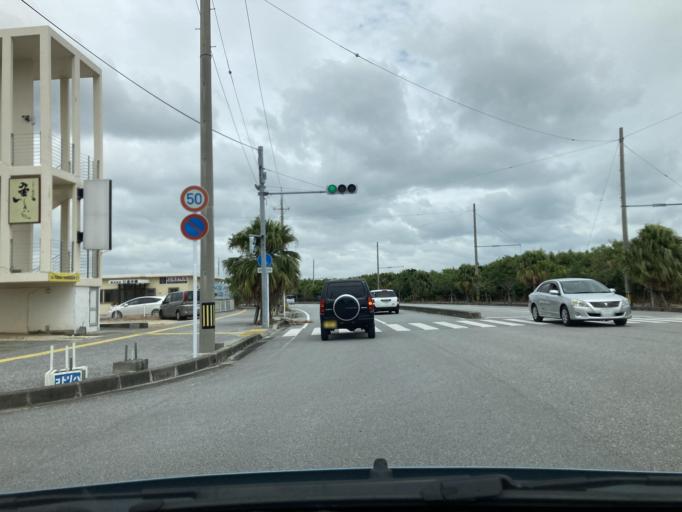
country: JP
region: Okinawa
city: Ginowan
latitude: 26.2093
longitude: 127.7641
